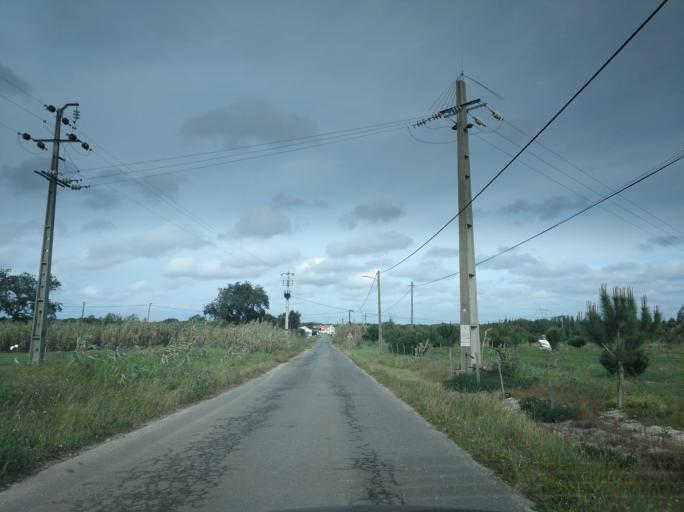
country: PT
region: Setubal
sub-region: Grandola
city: Grandola
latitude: 38.1956
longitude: -8.5494
